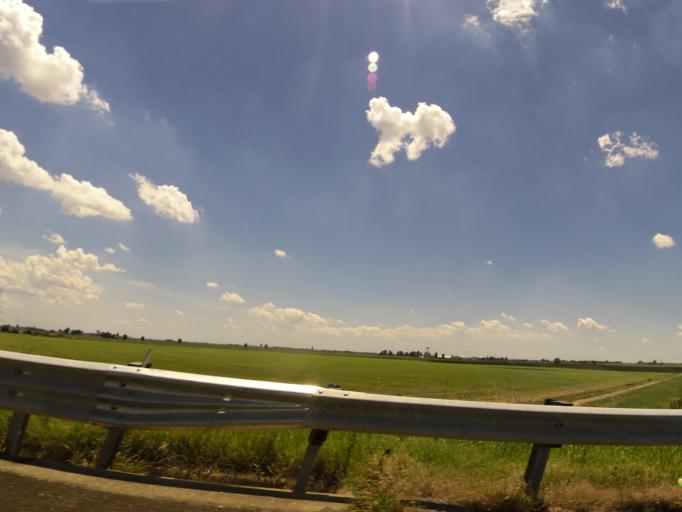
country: US
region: Missouri
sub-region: Pemiscot County
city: Caruthersville
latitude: 36.1835
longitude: -89.7014
